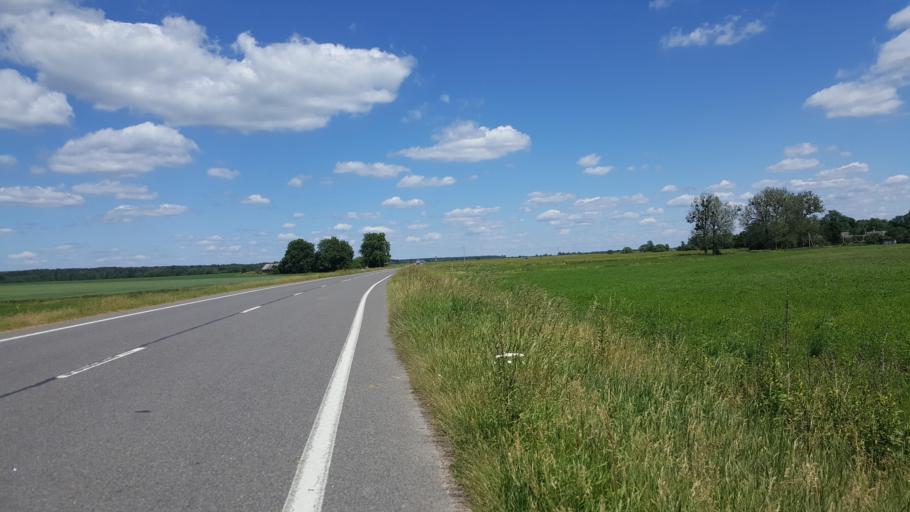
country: PL
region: Podlasie
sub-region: Powiat hajnowski
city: Czeremcha
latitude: 52.5031
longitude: 23.5010
